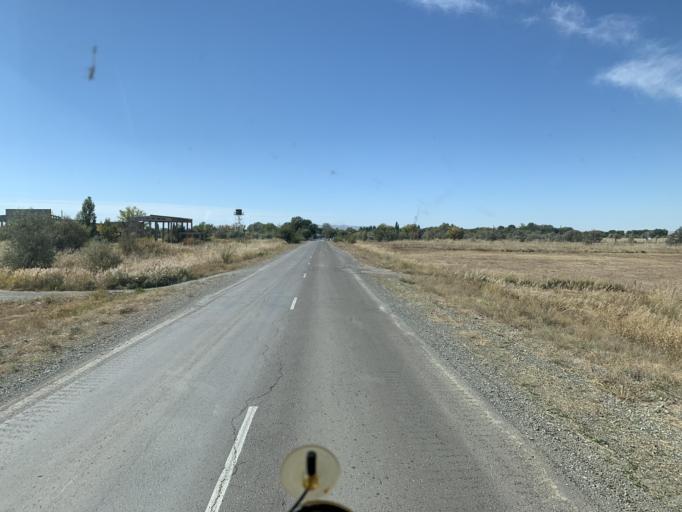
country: CN
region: Xinjiang Uygur Zizhiqu
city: Tacheng
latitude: 46.6638
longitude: 82.7510
